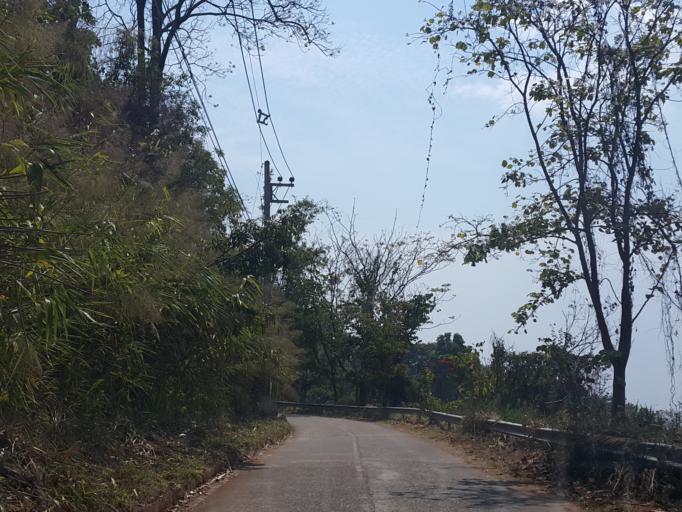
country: TH
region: Lampang
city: Mueang Pan
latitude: 18.8289
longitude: 99.3965
